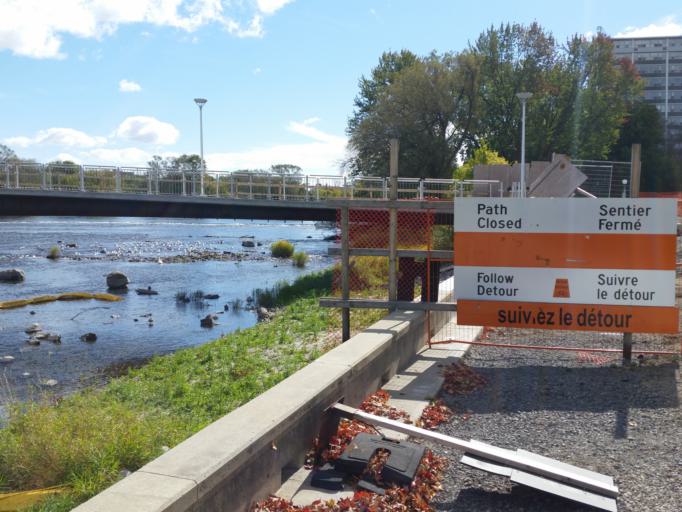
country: CA
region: Ontario
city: Ottawa
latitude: 45.4263
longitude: -75.6710
